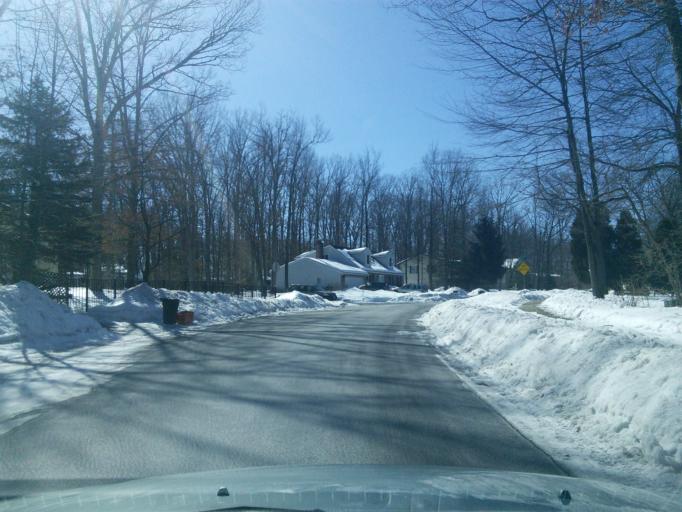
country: US
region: Pennsylvania
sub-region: Centre County
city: Park Forest Village
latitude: 40.8163
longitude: -77.8941
